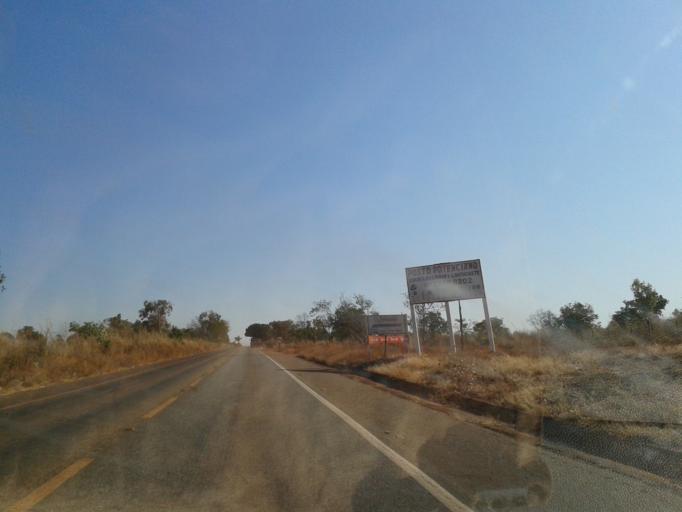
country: BR
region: Goias
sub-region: Mozarlandia
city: Mozarlandia
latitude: -14.7682
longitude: -50.5375
